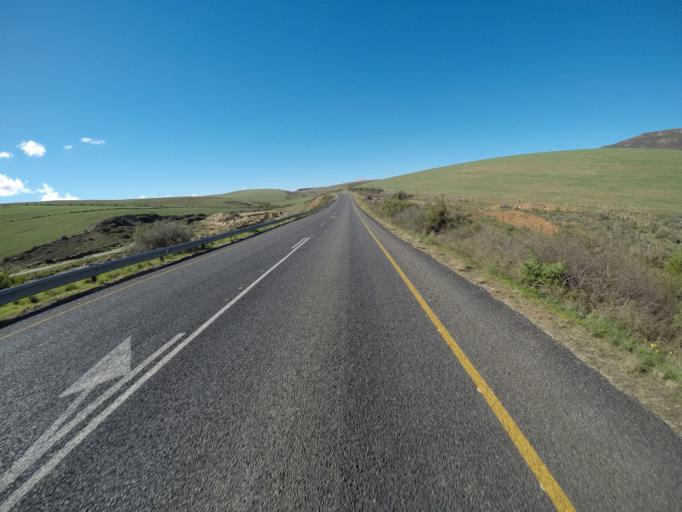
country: ZA
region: Western Cape
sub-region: Overberg District Municipality
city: Caledon
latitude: -34.1511
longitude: 19.4766
